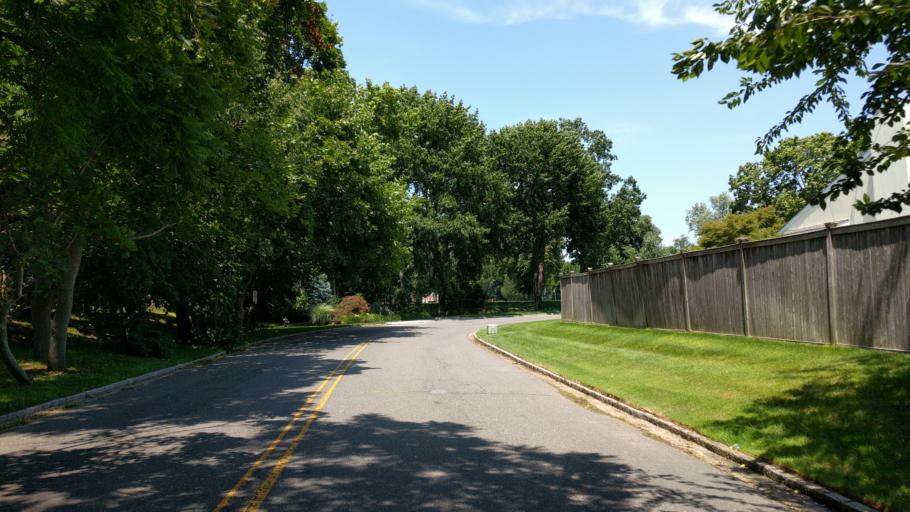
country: US
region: New York
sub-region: Nassau County
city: Syosset
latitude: 40.8190
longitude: -73.5145
